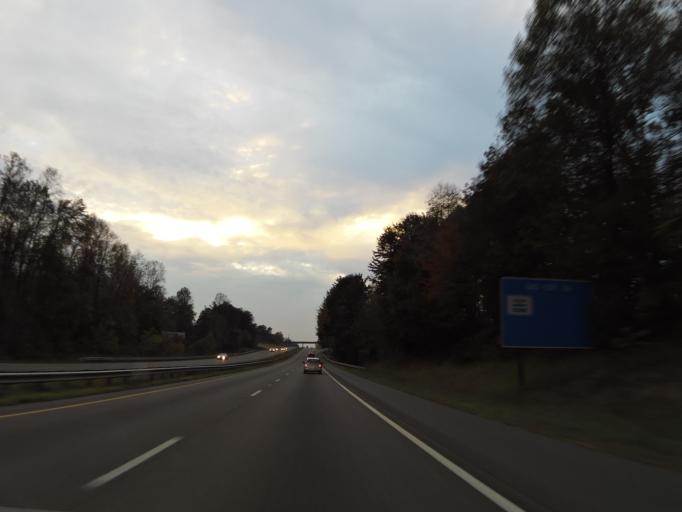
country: US
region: North Carolina
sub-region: Burke County
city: Drexel
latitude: 35.7265
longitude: -81.6298
